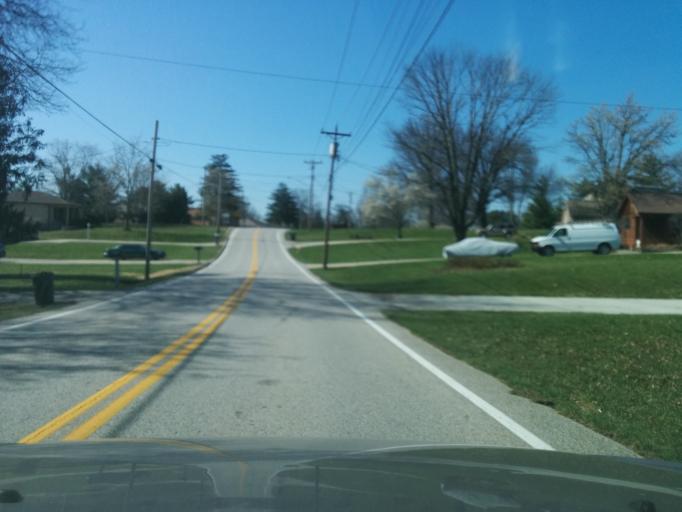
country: US
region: Ohio
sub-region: Hamilton County
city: Cheviot
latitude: 39.1807
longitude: -84.6217
